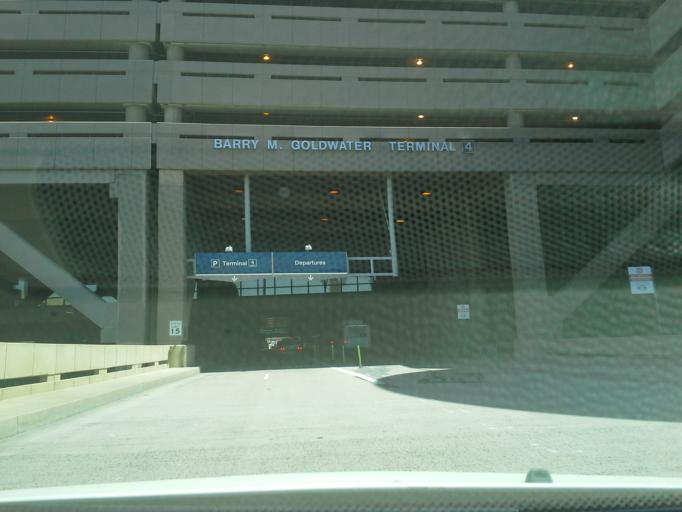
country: US
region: Arizona
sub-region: Maricopa County
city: Tempe Junction
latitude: 33.4359
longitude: -112.0001
